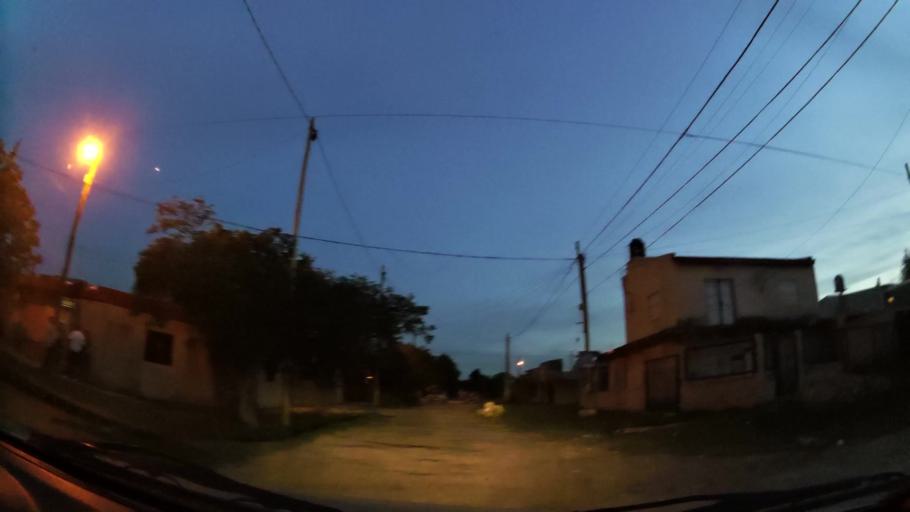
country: AR
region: Buenos Aires
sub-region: Partido de Almirante Brown
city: Adrogue
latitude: -34.8079
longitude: -58.2921
